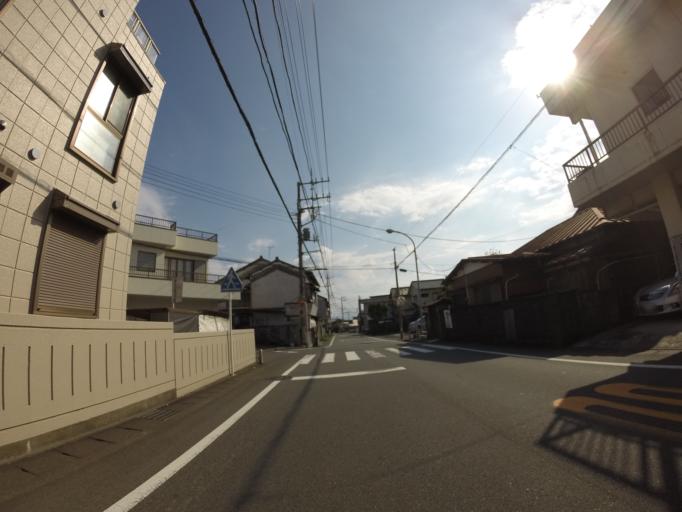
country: JP
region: Shizuoka
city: Fujinomiya
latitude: 35.1890
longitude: 138.6456
